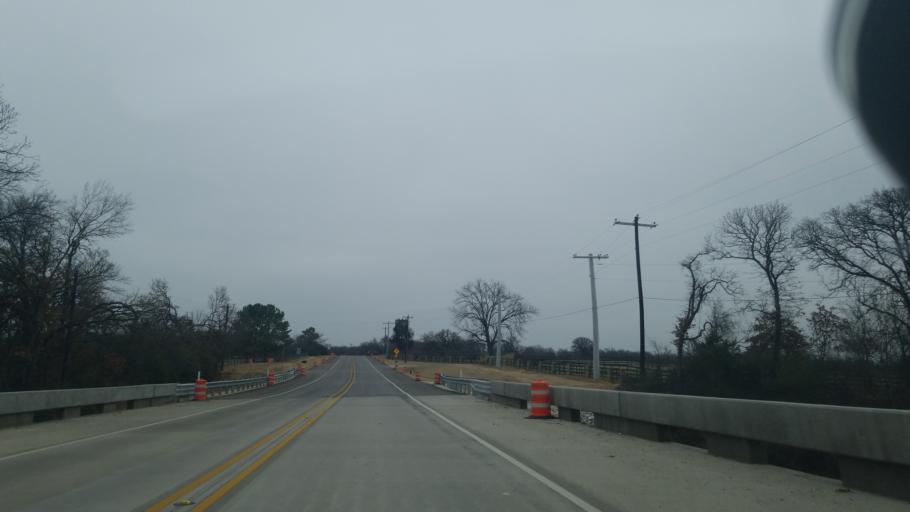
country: US
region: Texas
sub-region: Denton County
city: Argyle
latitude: 33.1248
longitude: -97.1395
